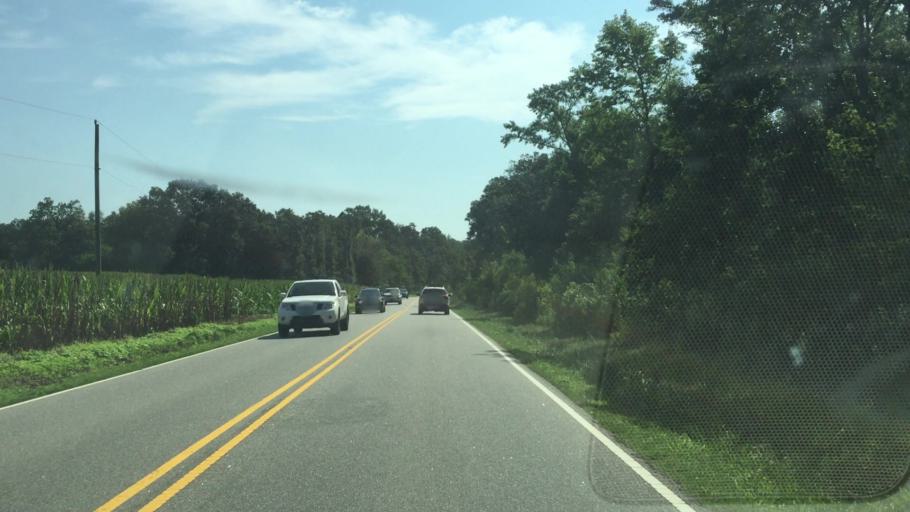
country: US
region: North Carolina
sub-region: Stanly County
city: Oakboro
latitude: 35.1335
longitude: -80.3841
